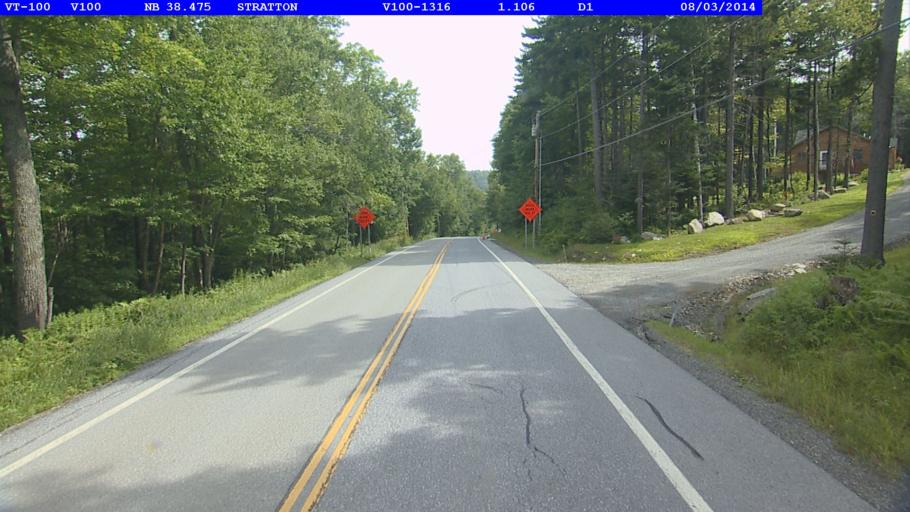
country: US
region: Vermont
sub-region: Windham County
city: Dover
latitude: 43.0060
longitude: -72.8814
